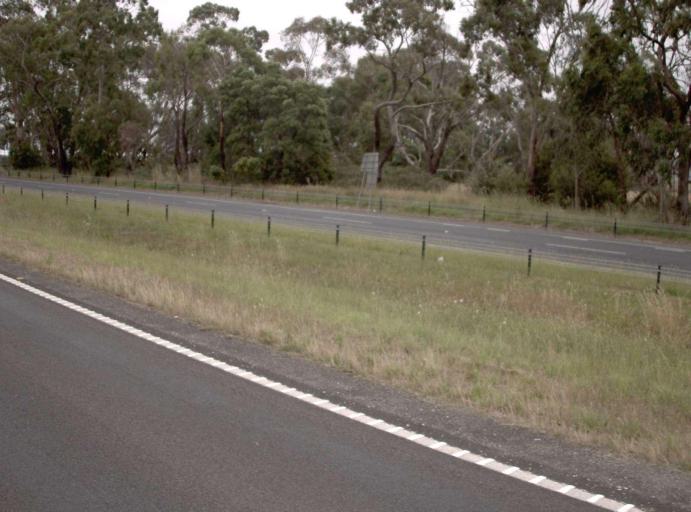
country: AU
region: Victoria
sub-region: Latrobe
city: Traralgon
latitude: -38.2149
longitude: 146.4807
